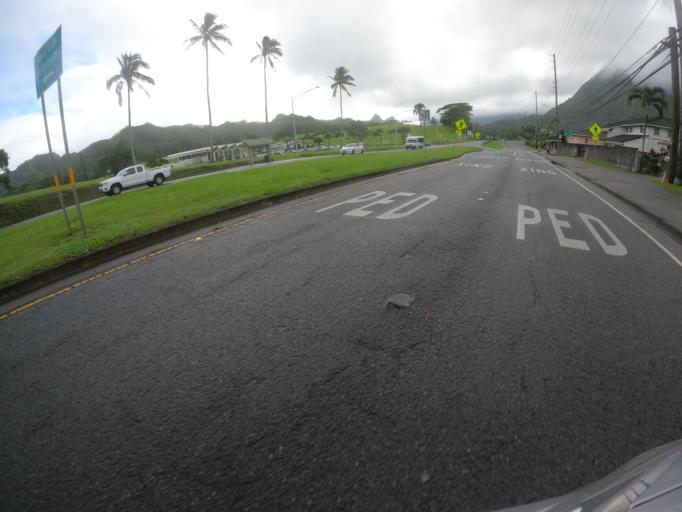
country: US
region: Hawaii
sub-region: Honolulu County
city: Kane'ohe
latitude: 21.3898
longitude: -157.7951
